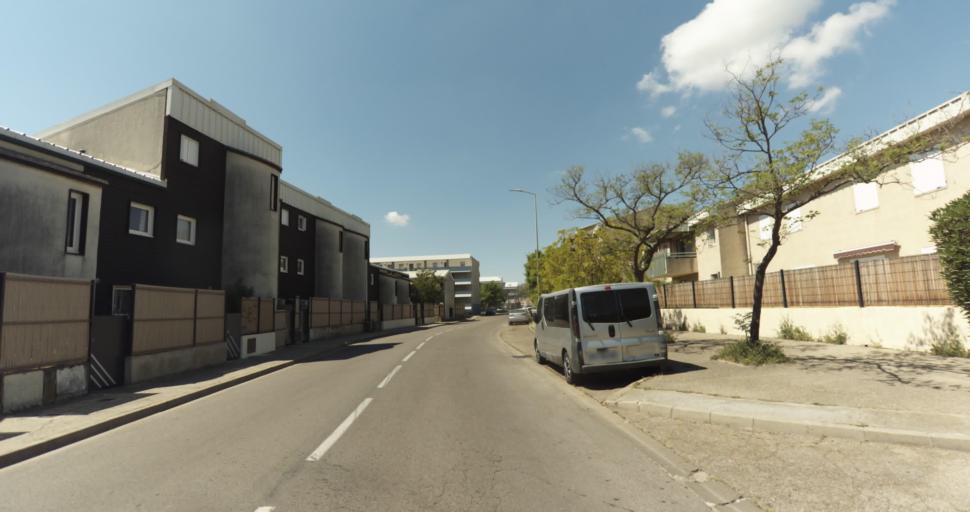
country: FR
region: Languedoc-Roussillon
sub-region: Departement du Gard
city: Milhaud
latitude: 43.8164
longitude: 4.3224
